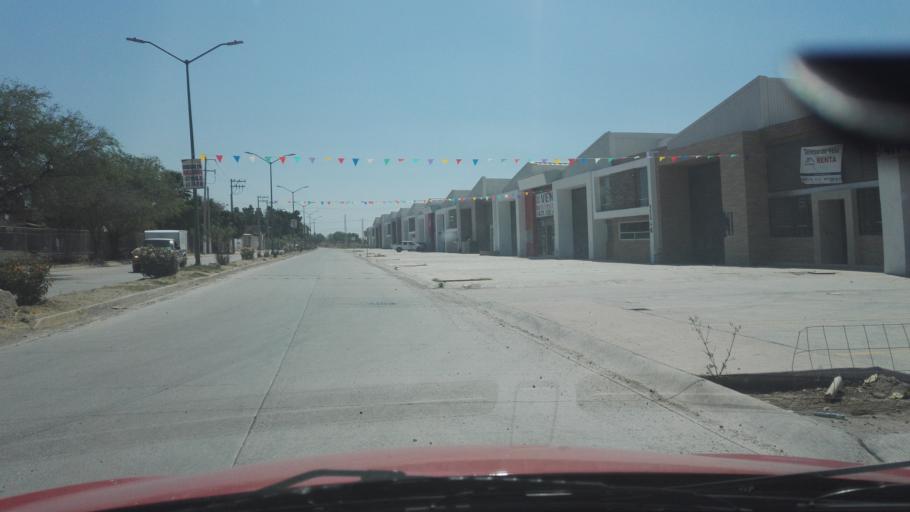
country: MX
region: Guanajuato
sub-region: Leon
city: Fraccionamiento Paraiso Real
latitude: 21.0896
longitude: -101.5945
